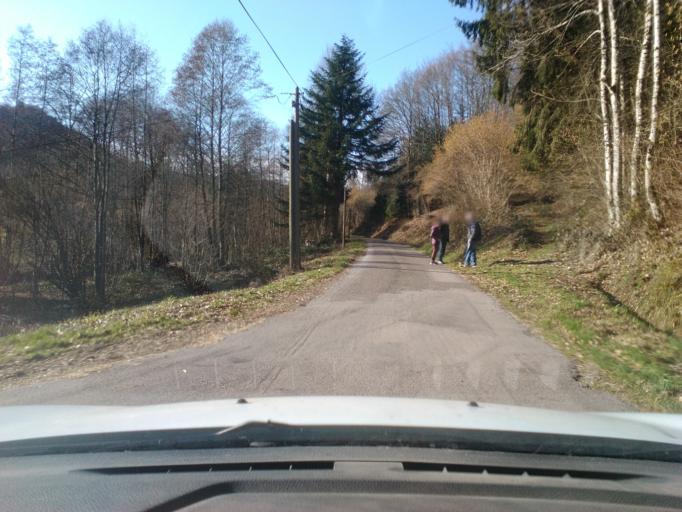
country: FR
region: Lorraine
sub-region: Departement des Vosges
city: Vecoux
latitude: 47.9737
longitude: 6.6602
